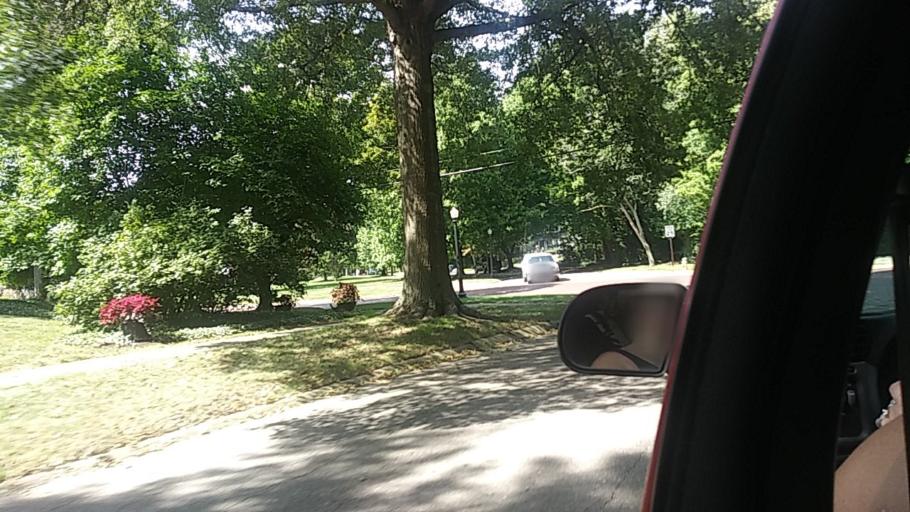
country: US
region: Ohio
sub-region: Summit County
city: Akron
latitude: 41.0993
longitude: -81.5582
